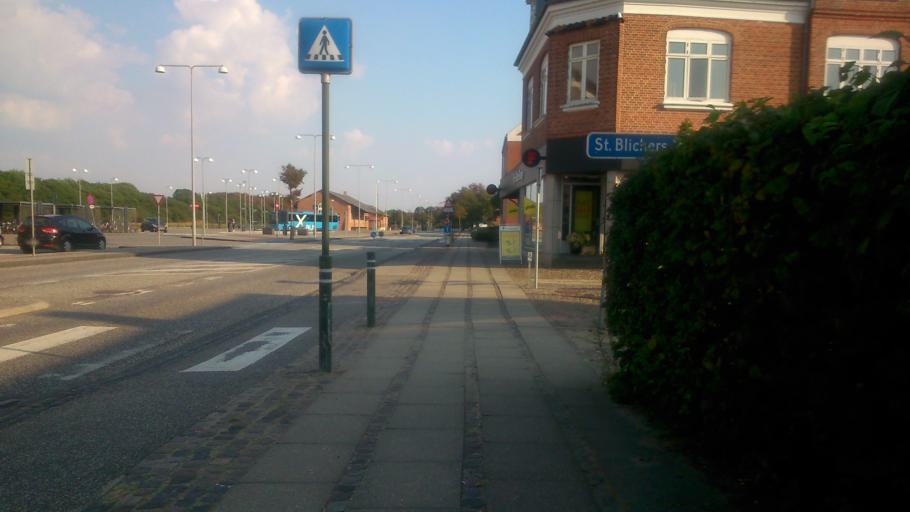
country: DK
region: Central Jutland
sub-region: Ringkobing-Skjern Kommune
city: Ringkobing
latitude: 56.0929
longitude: 8.2494
